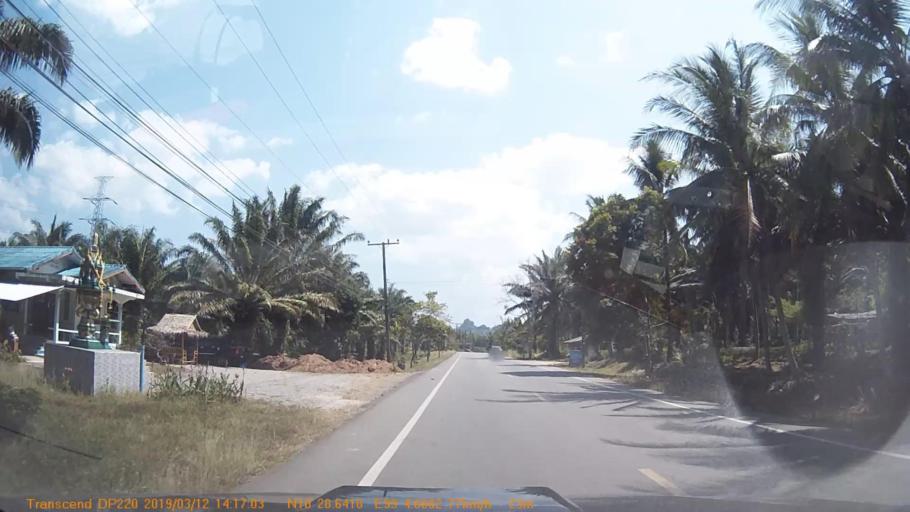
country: TH
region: Chumphon
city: Chumphon
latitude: 10.4771
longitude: 99.0778
